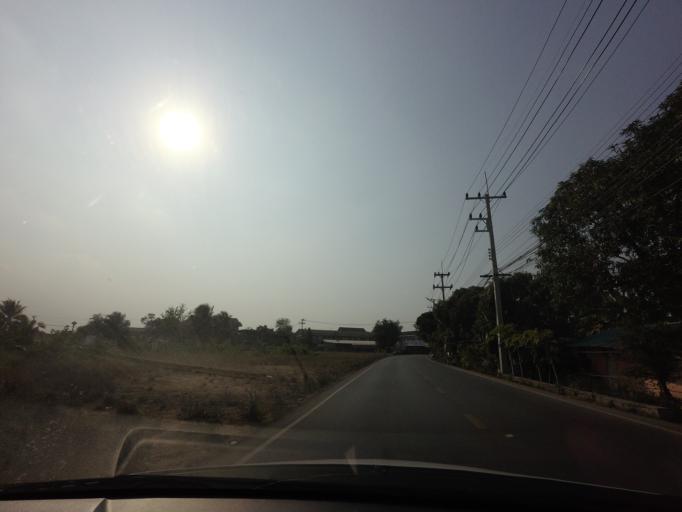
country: TH
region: Samut Sakhon
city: Krathum Baen
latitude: 13.6945
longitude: 100.2479
